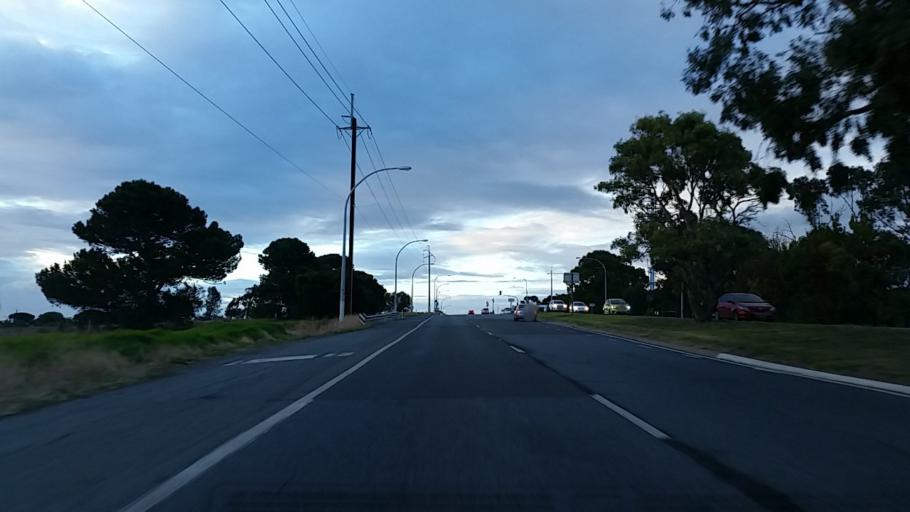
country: AU
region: South Australia
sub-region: Marion
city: Trott Park
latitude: -35.0571
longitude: 138.5351
